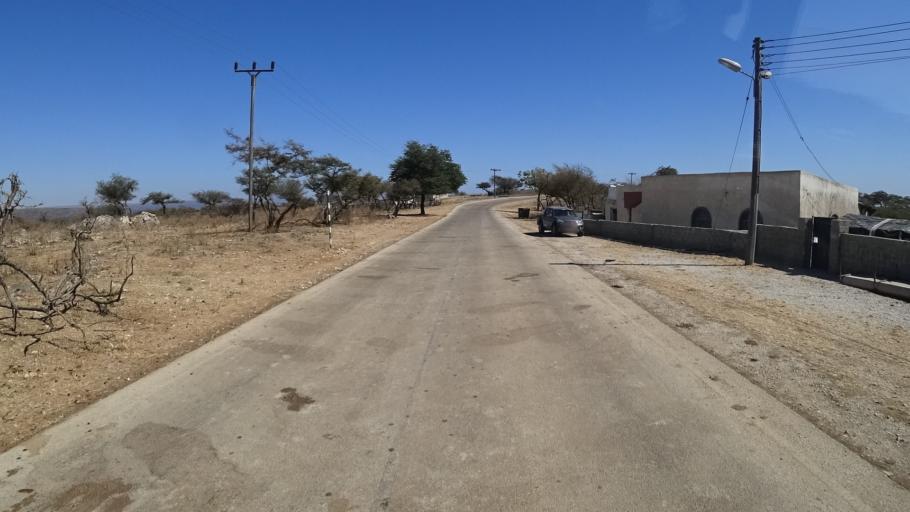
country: YE
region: Al Mahrah
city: Hawf
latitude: 16.7786
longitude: 53.3353
